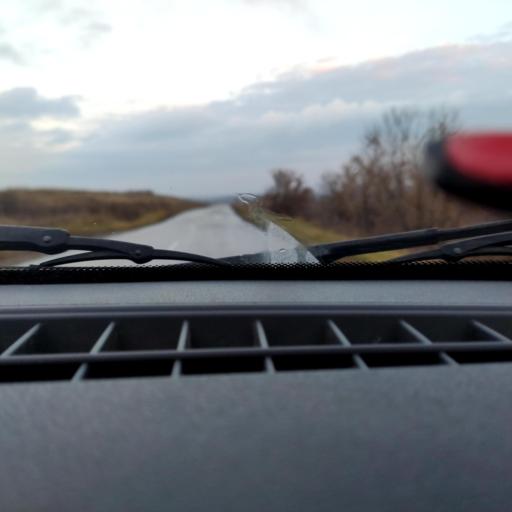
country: RU
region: Bashkortostan
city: Avdon
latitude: 54.5112
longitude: 55.8505
